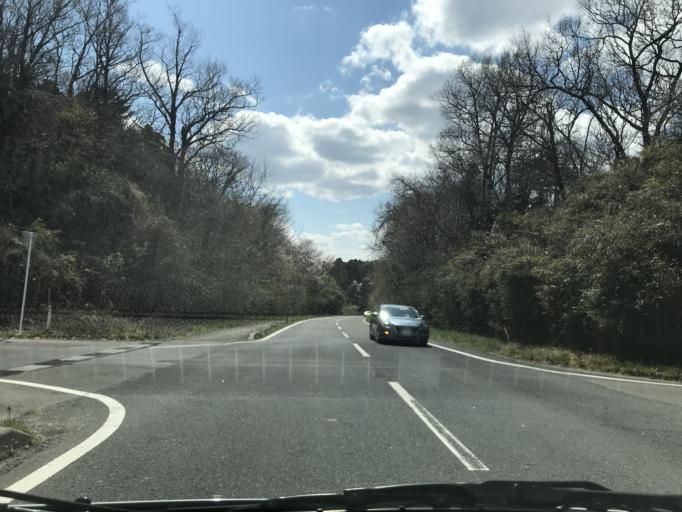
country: JP
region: Miyagi
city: Wakuya
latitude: 38.6304
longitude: 141.2208
